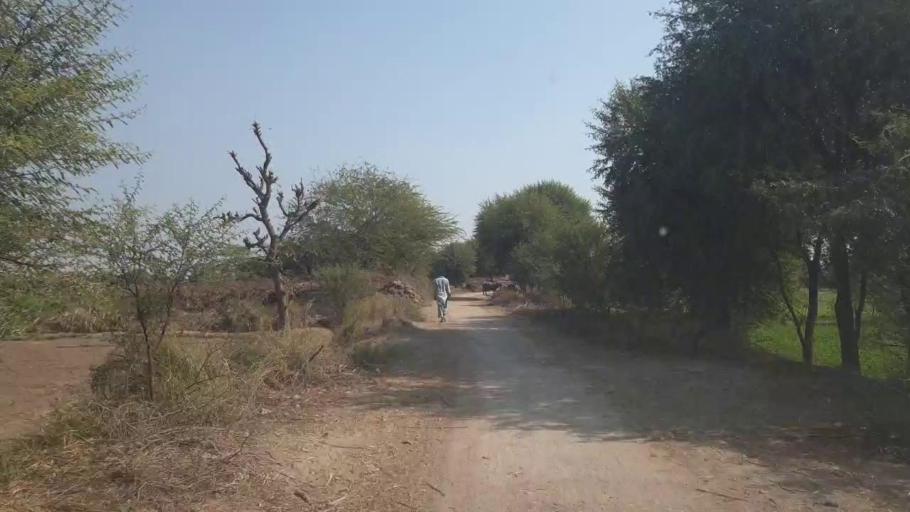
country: PK
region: Sindh
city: Tando Allahyar
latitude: 25.4420
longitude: 68.8661
